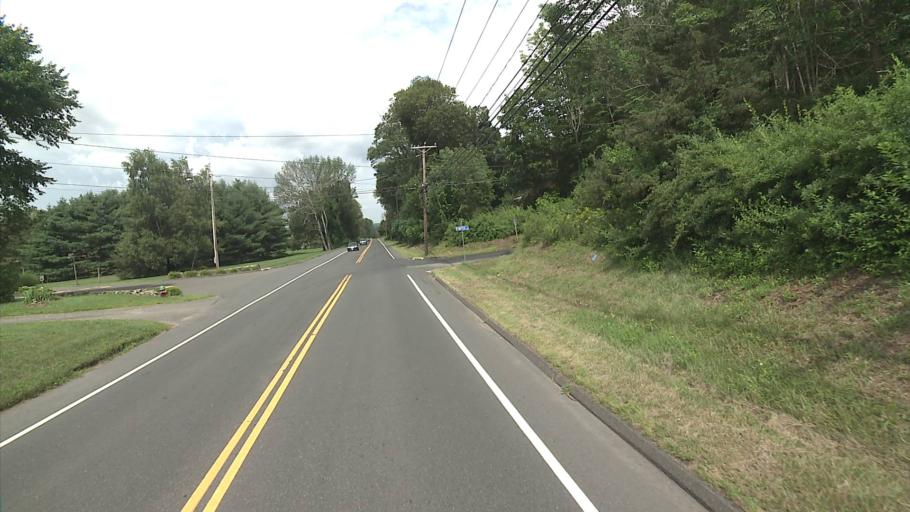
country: US
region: Connecticut
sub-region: New Haven County
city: Southbury
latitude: 41.4725
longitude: -73.1855
